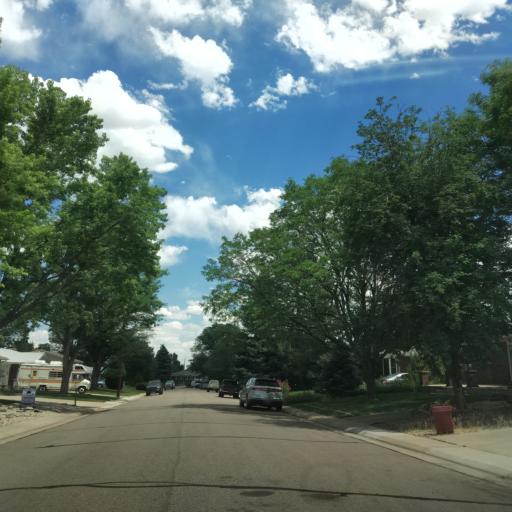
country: US
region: Colorado
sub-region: Jefferson County
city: Lakewood
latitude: 39.6887
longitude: -105.0845
